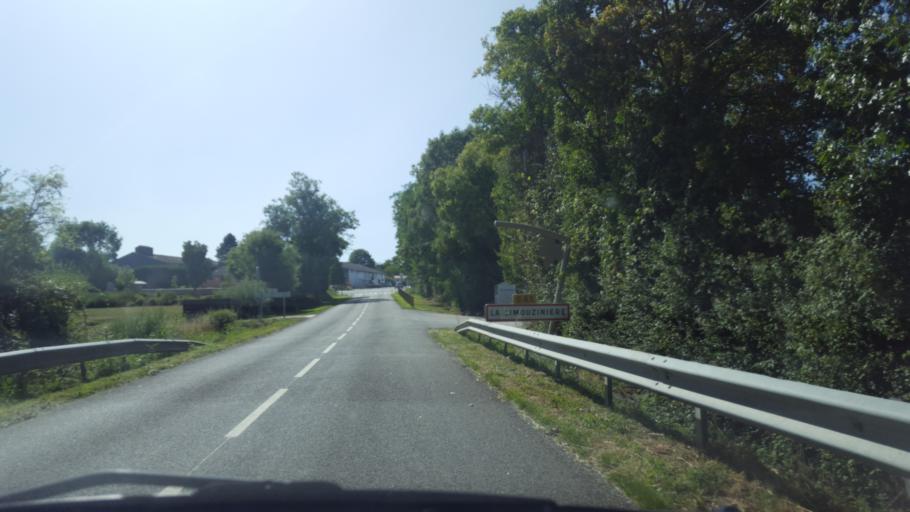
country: FR
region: Pays de la Loire
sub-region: Departement de la Loire-Atlantique
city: La Limouziniere
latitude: 46.9920
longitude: -1.5917
